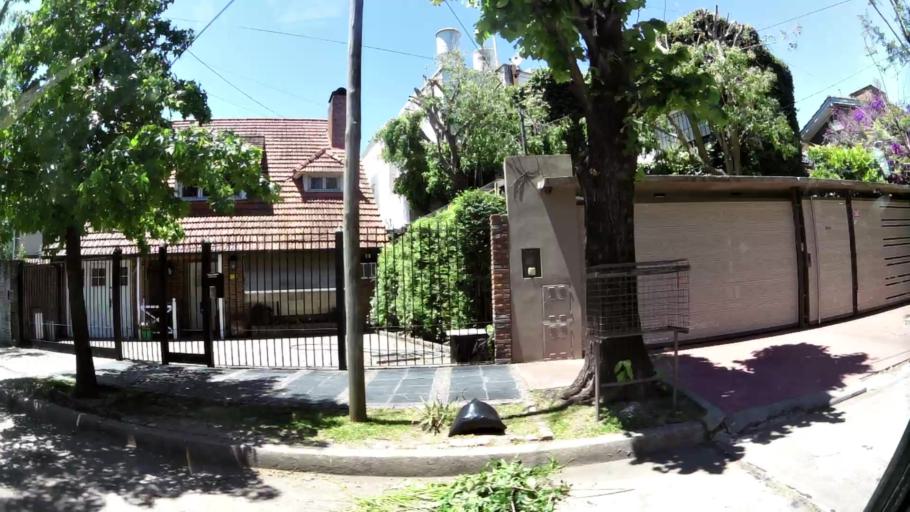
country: AR
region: Buenos Aires
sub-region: Partido de San Isidro
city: San Isidro
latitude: -34.4774
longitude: -58.5048
